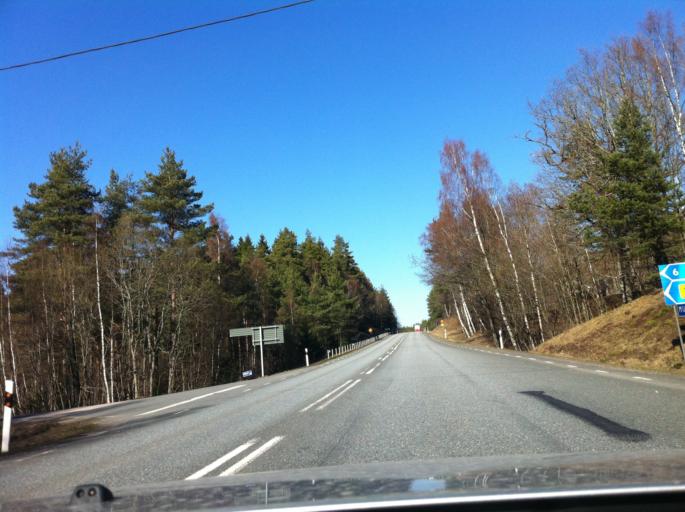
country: SE
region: Joenkoeping
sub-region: Mullsjo Kommun
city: Mullsjoe
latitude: 57.9715
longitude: 13.8326
